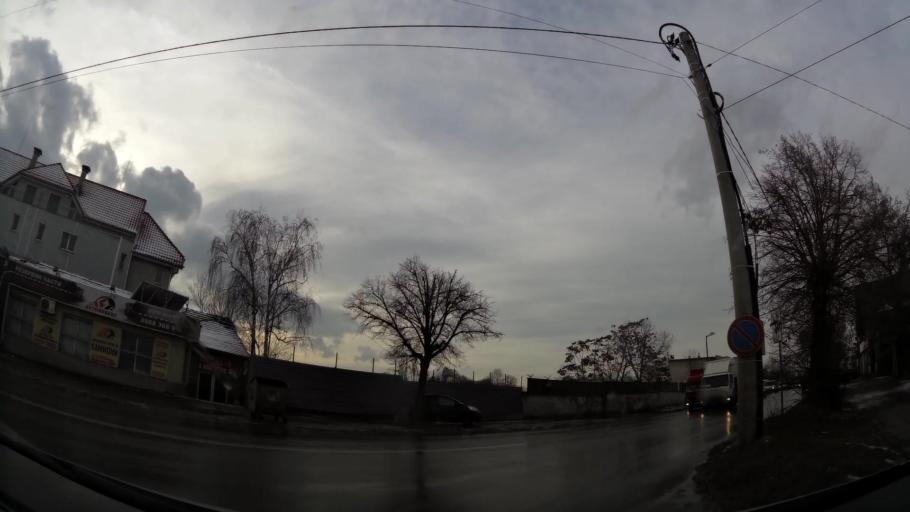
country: BG
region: Sofia-Capital
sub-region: Stolichna Obshtina
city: Sofia
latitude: 42.7147
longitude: 23.3416
